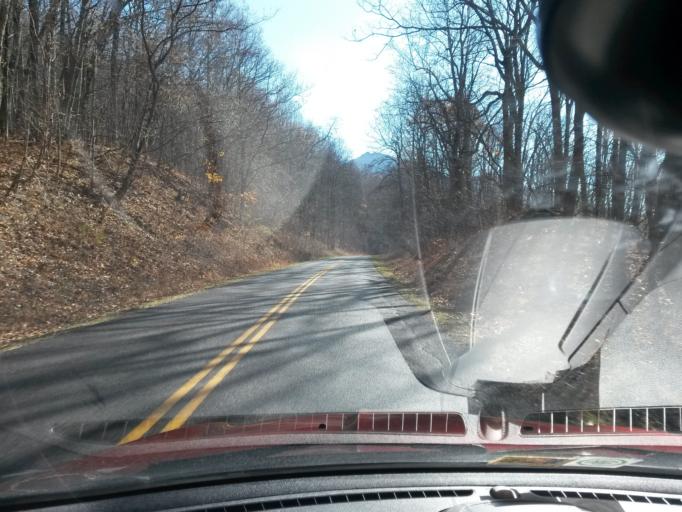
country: US
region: Virginia
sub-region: Botetourt County
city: Buchanan
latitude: 37.4481
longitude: -79.6193
